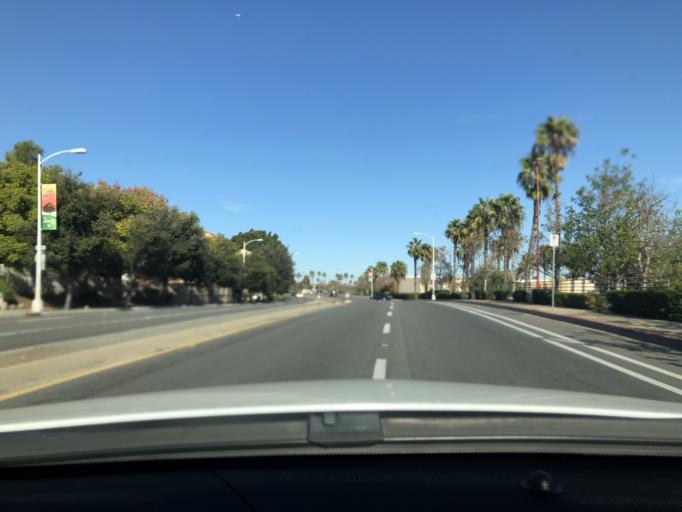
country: US
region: California
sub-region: San Diego County
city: Lemon Grove
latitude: 32.7383
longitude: -117.0581
